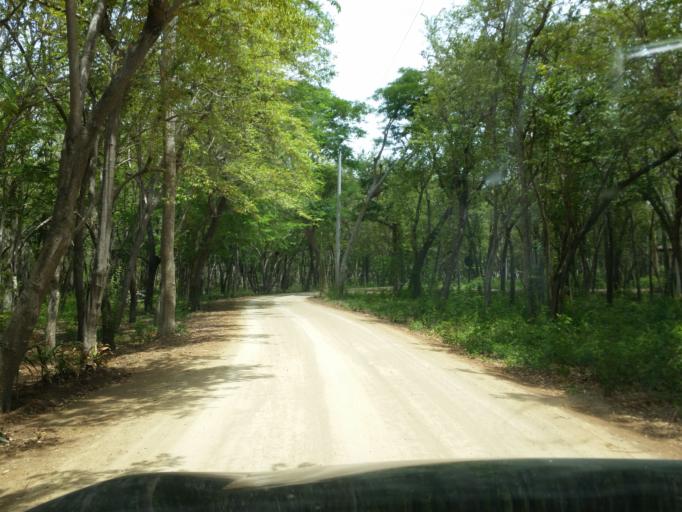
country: NI
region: Rivas
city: Tola
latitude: 11.4113
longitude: -86.0466
